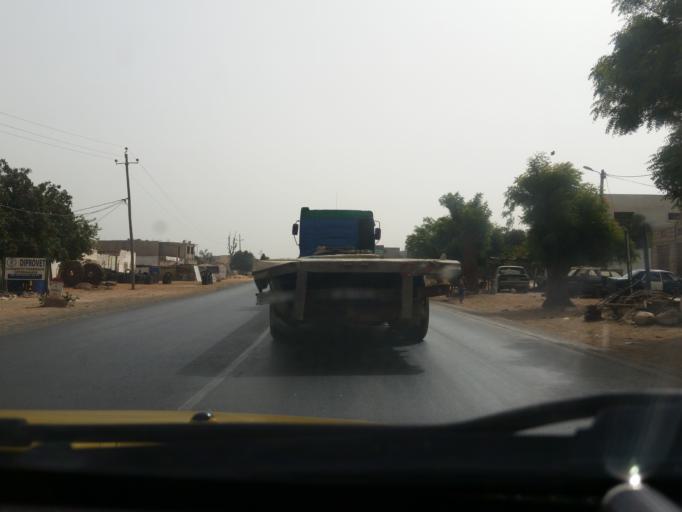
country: SN
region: Thies
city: Pout
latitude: 14.7419
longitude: -17.1376
